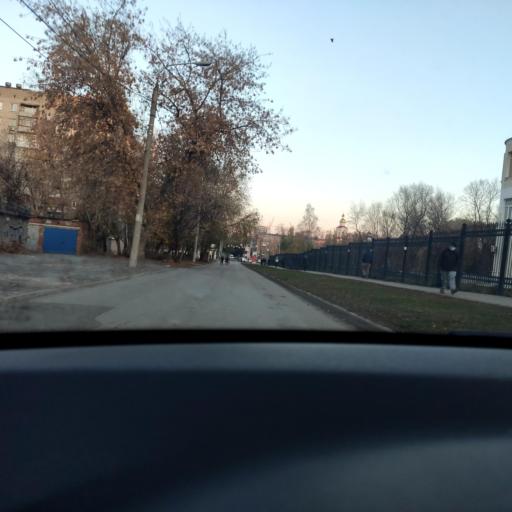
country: RU
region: Samara
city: Samara
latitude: 53.2028
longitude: 50.1658
